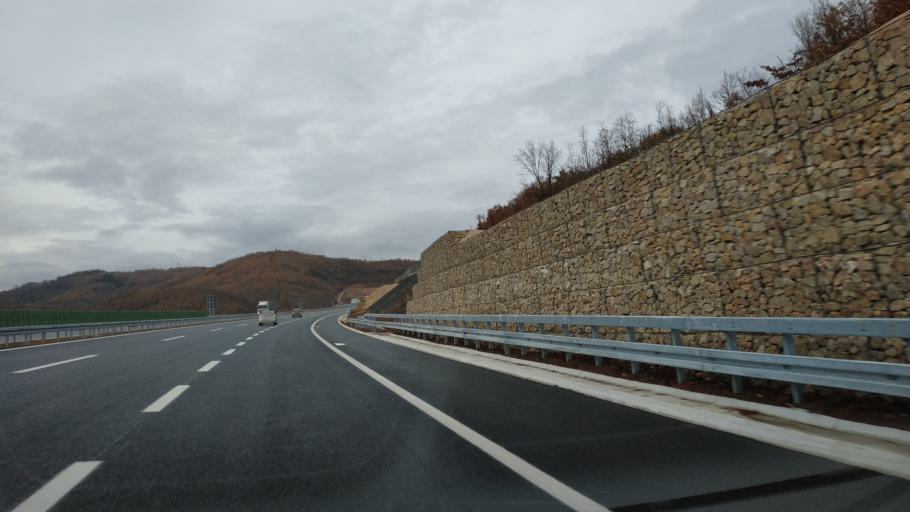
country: RS
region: Central Serbia
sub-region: Nisavski Okrug
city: Gadzin Han
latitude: 43.2602
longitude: 22.1462
